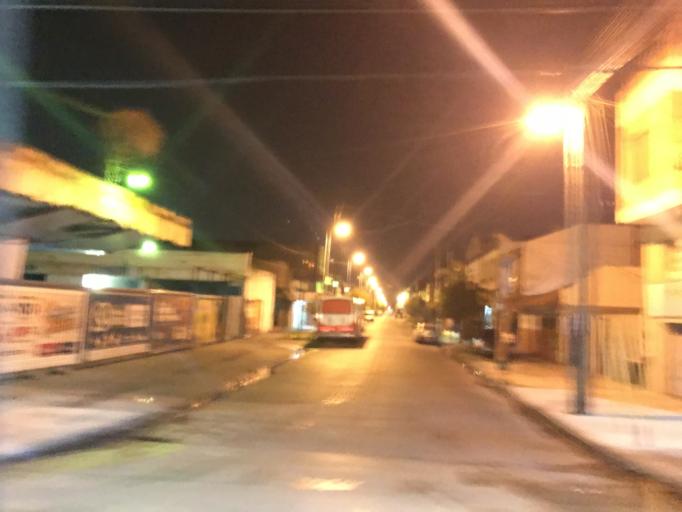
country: AR
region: Buenos Aires
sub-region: Partido de Lanus
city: Lanus
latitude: -34.6812
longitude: -58.4181
